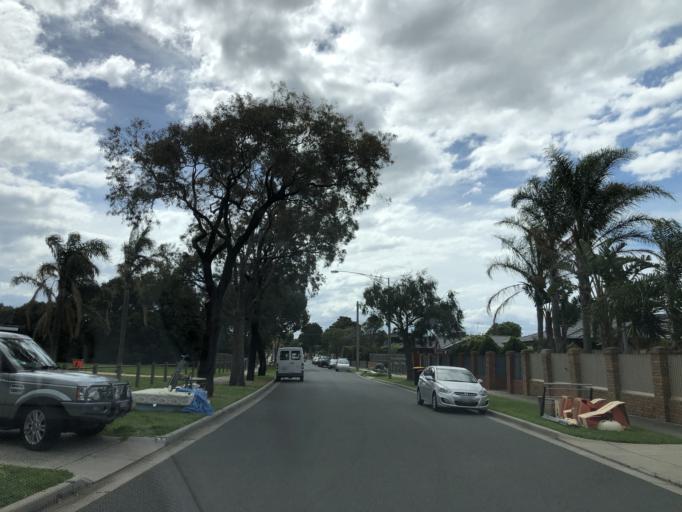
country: AU
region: Victoria
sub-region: Kingston
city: Carrum
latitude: -38.0760
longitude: 145.1349
